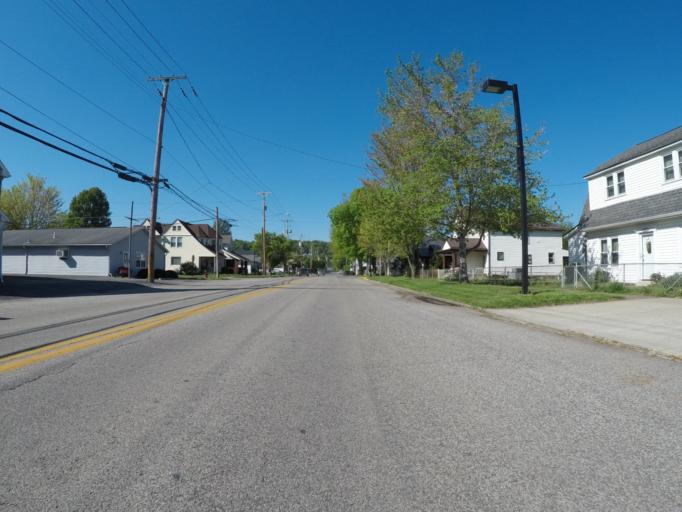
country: US
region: West Virginia
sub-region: Wayne County
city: Ceredo
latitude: 38.3951
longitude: -82.5590
